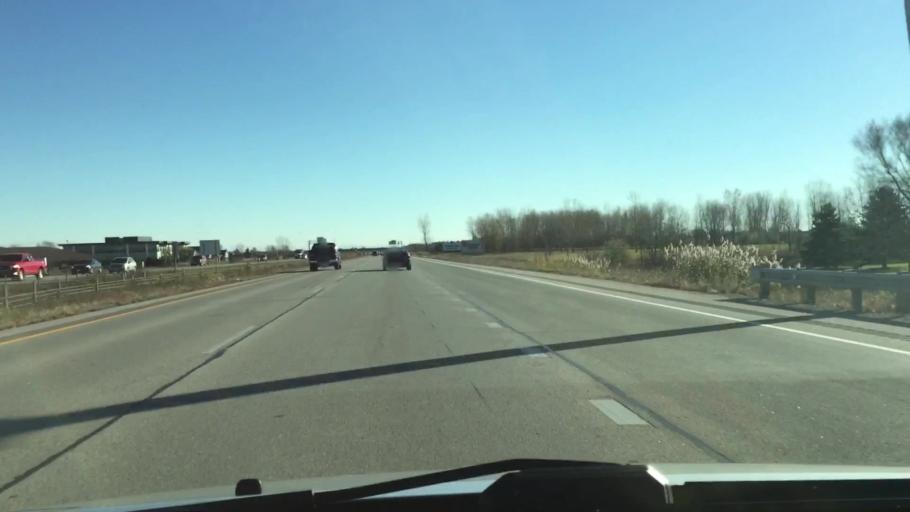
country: US
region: Wisconsin
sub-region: Outagamie County
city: Kimberly
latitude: 44.2980
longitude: -88.3698
